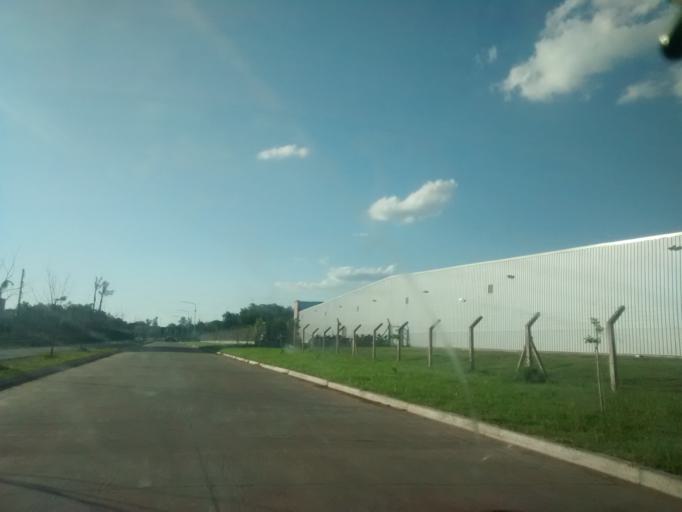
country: AR
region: Chaco
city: Fontana
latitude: -27.4481
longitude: -59.0206
